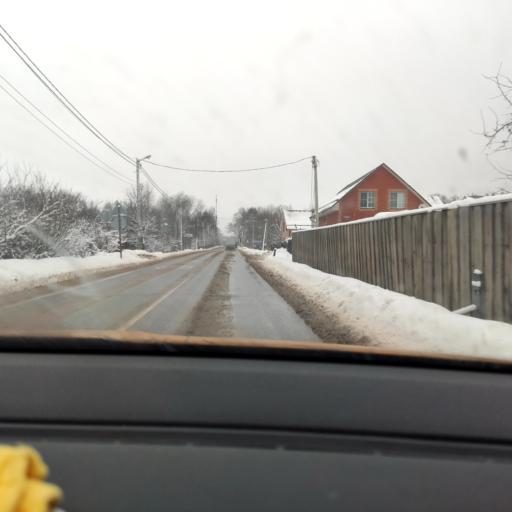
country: RU
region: Moskovskaya
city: Yershovo
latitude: 55.7534
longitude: 36.8706
